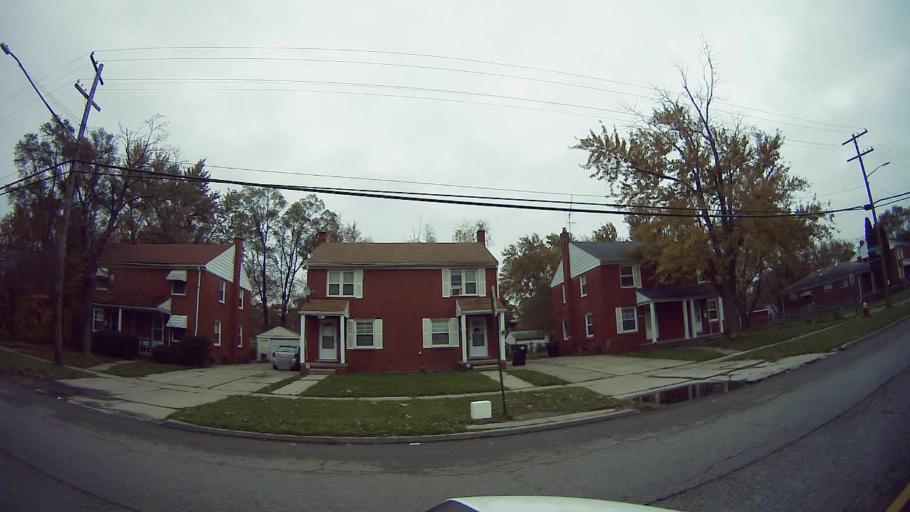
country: US
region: Michigan
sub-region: Wayne County
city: Dearborn Heights
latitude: 42.3614
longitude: -83.2360
